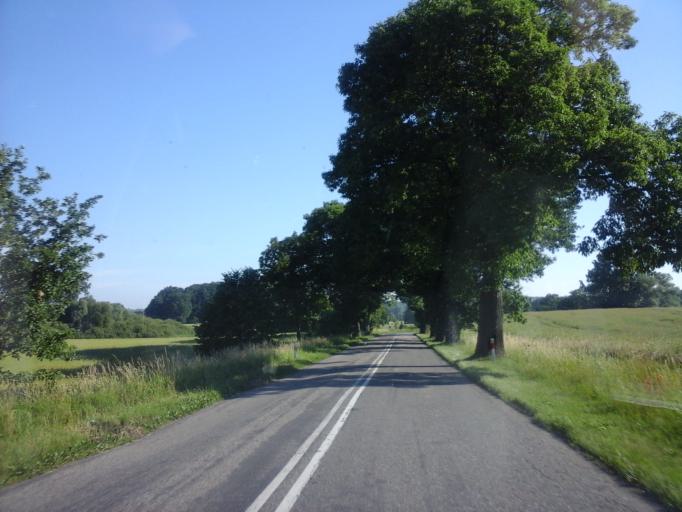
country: PL
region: West Pomeranian Voivodeship
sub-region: Powiat choszczenski
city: Recz
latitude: 53.3231
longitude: 15.5702
